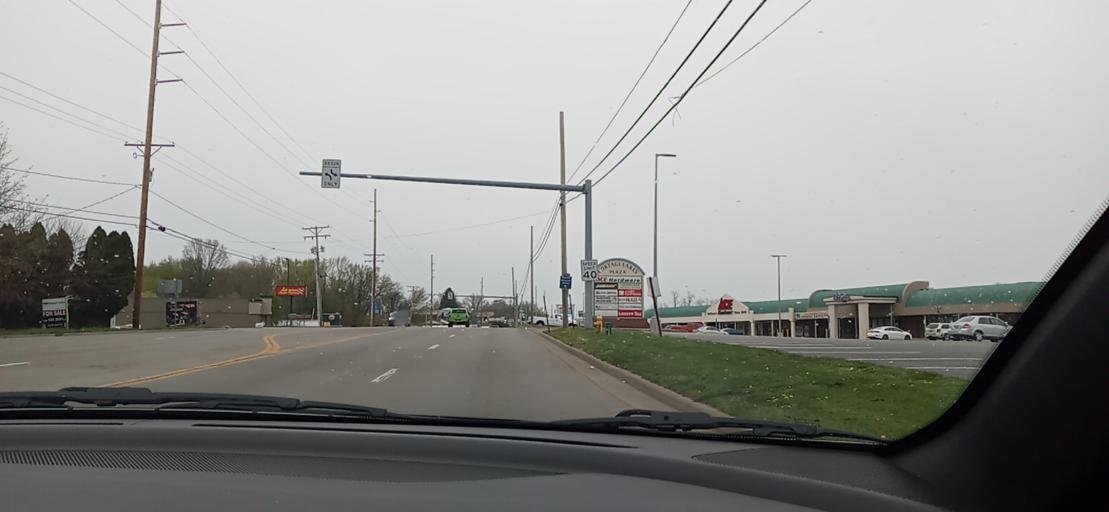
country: US
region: Ohio
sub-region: Summit County
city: Portage Lakes
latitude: 41.0113
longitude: -81.5544
